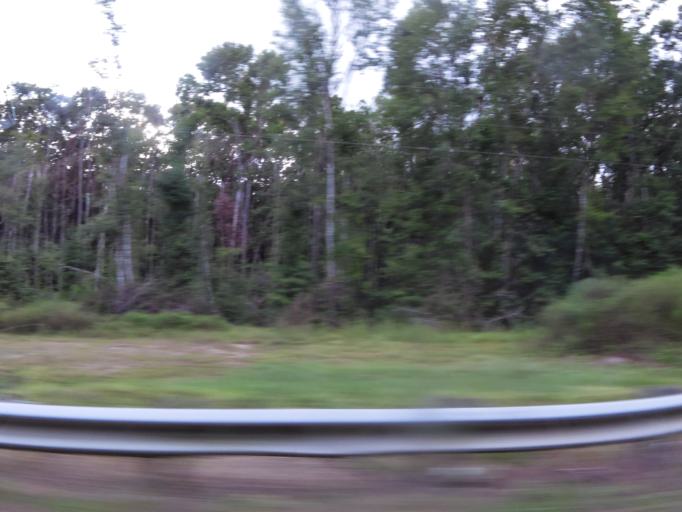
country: US
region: Georgia
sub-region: Liberty County
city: Midway
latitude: 31.8213
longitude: -81.4298
